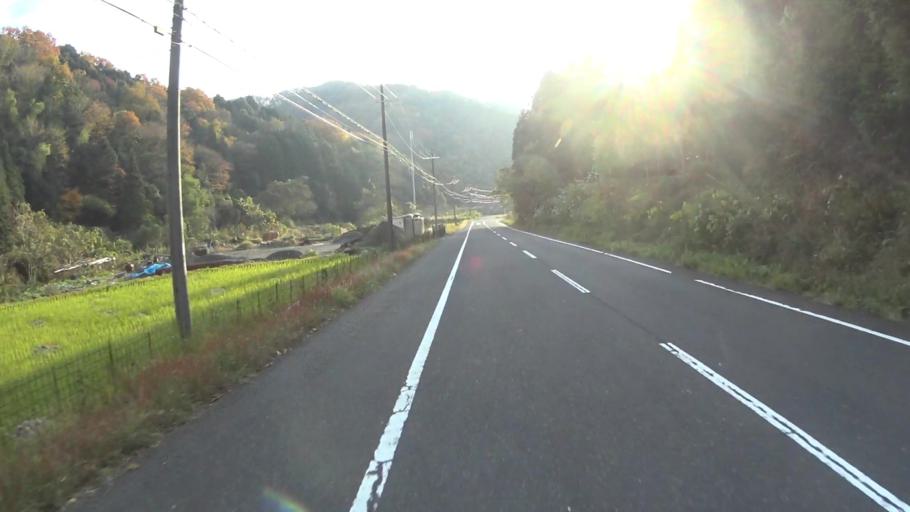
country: JP
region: Kyoto
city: Maizuru
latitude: 35.5097
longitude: 135.4531
